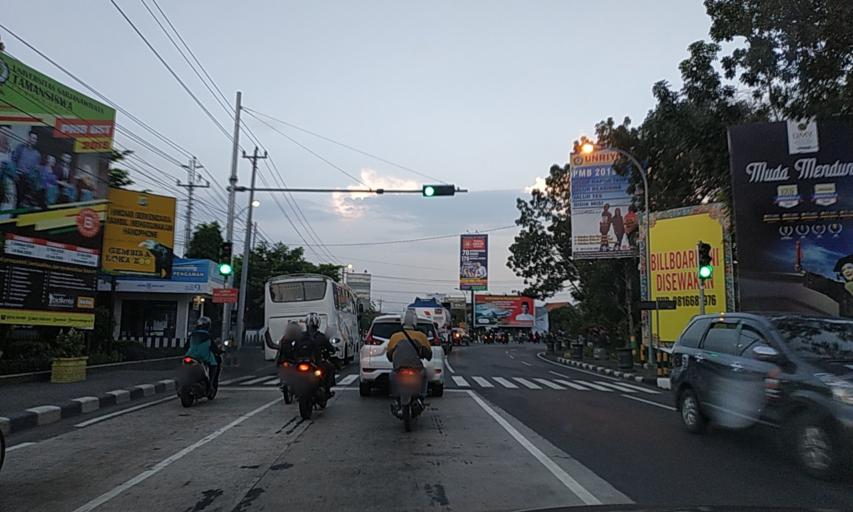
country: ID
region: Daerah Istimewa Yogyakarta
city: Srandakan
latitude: -7.8651
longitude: 110.1512
